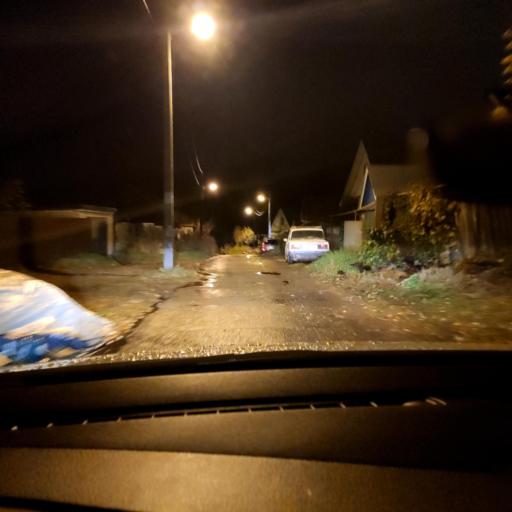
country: RU
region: Tatarstan
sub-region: Gorod Kazan'
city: Kazan
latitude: 55.8381
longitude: 49.2078
